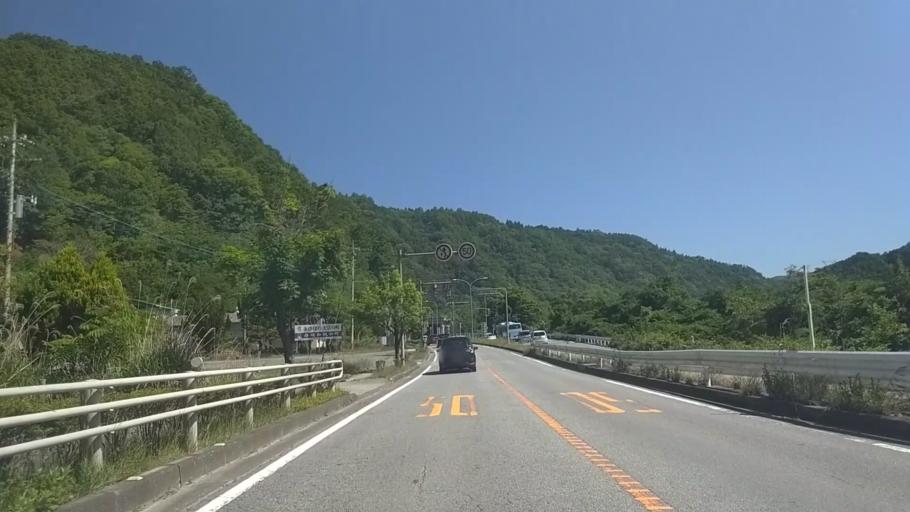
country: JP
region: Yamanashi
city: Ryuo
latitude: 35.4987
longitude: 138.4460
